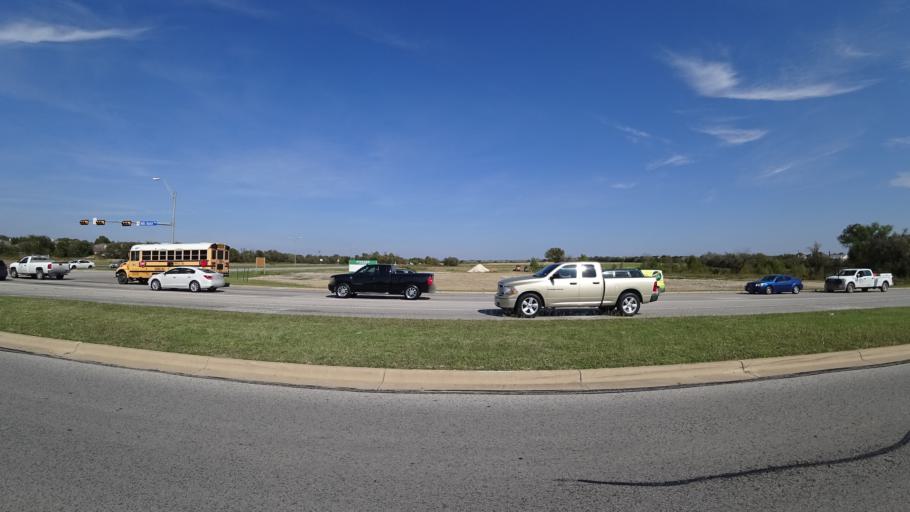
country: US
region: Texas
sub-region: Travis County
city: Pflugerville
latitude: 30.4245
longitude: -97.6260
